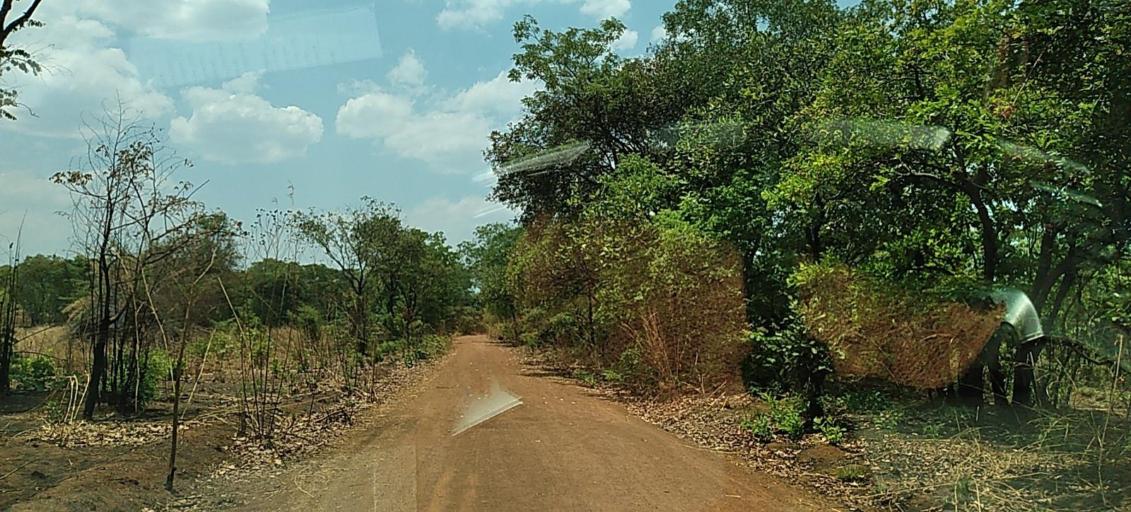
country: ZM
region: Copperbelt
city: Chingola
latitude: -12.5465
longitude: 27.6316
